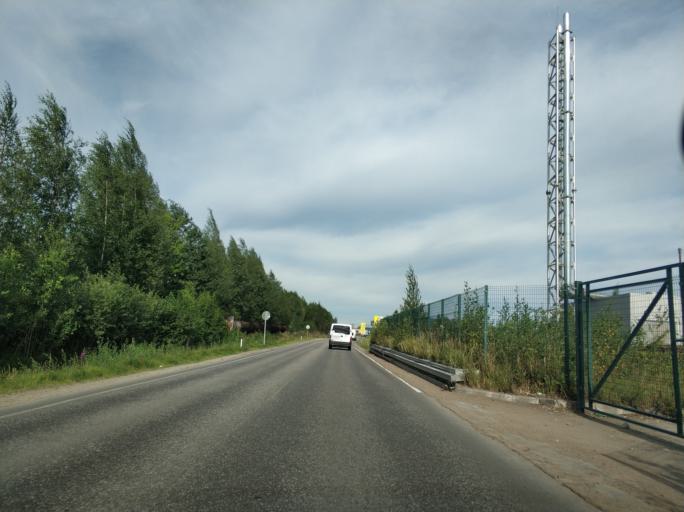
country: RU
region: St.-Petersburg
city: Grazhdanka
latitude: 60.0467
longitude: 30.4164
